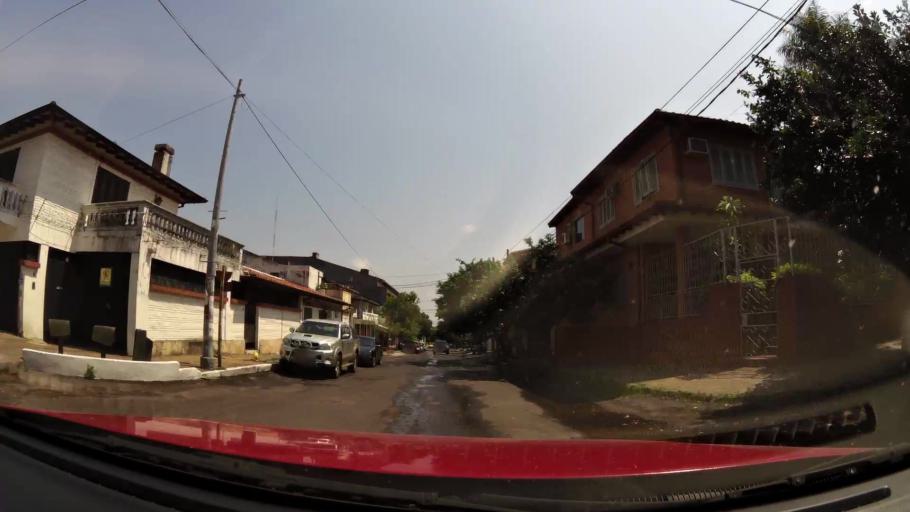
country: PY
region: Presidente Hayes
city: Nanawa
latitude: -25.2834
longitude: -57.6532
